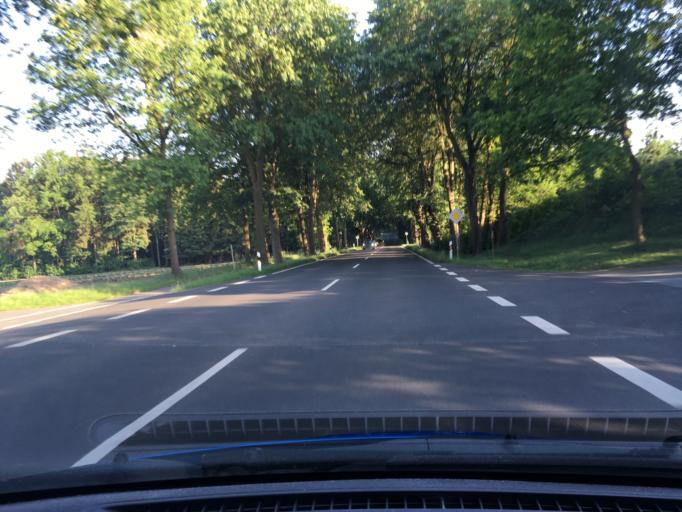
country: DE
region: Lower Saxony
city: Welle
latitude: 53.2305
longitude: 9.8051
